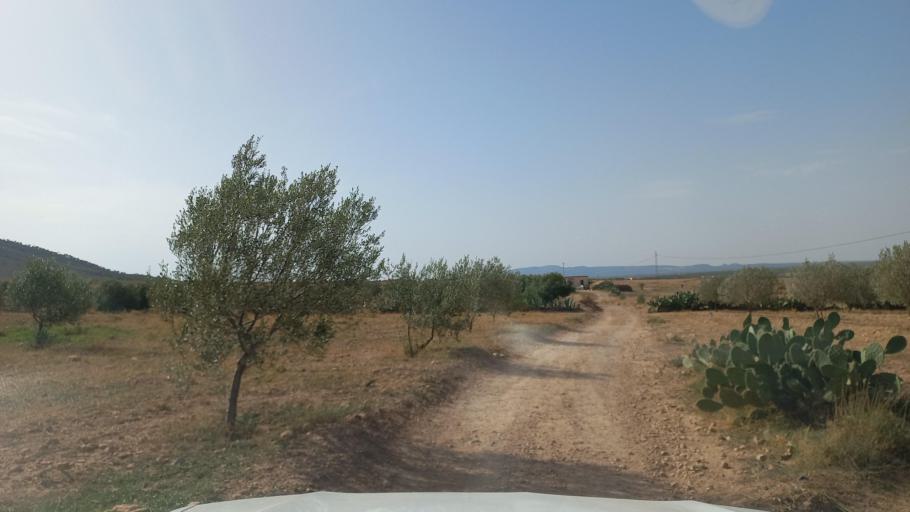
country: TN
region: Al Qasrayn
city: Kasserine
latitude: 35.3386
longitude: 8.8211
